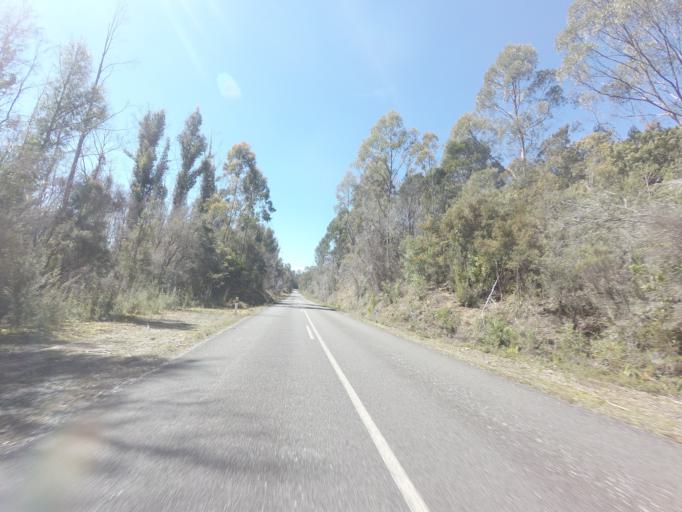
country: AU
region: Tasmania
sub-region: Huon Valley
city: Geeveston
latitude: -42.8352
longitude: 146.2668
